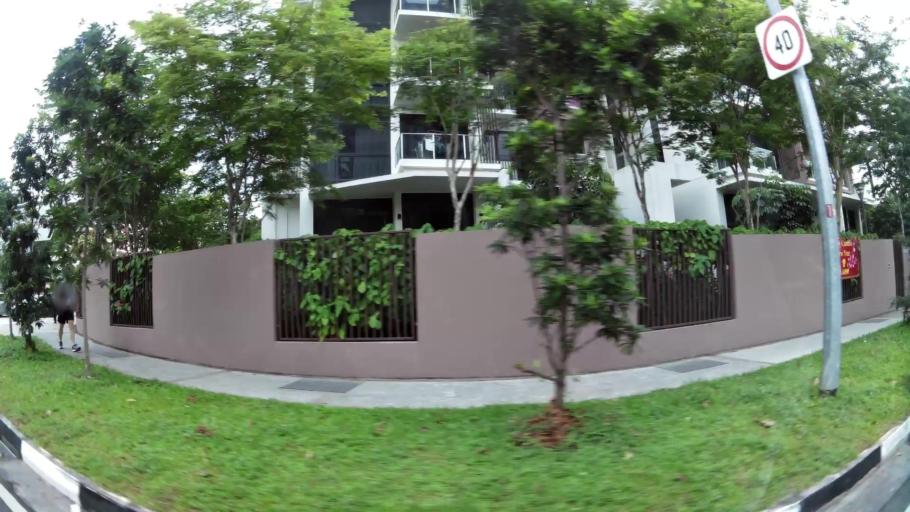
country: SG
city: Singapore
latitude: 1.3323
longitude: 103.8697
